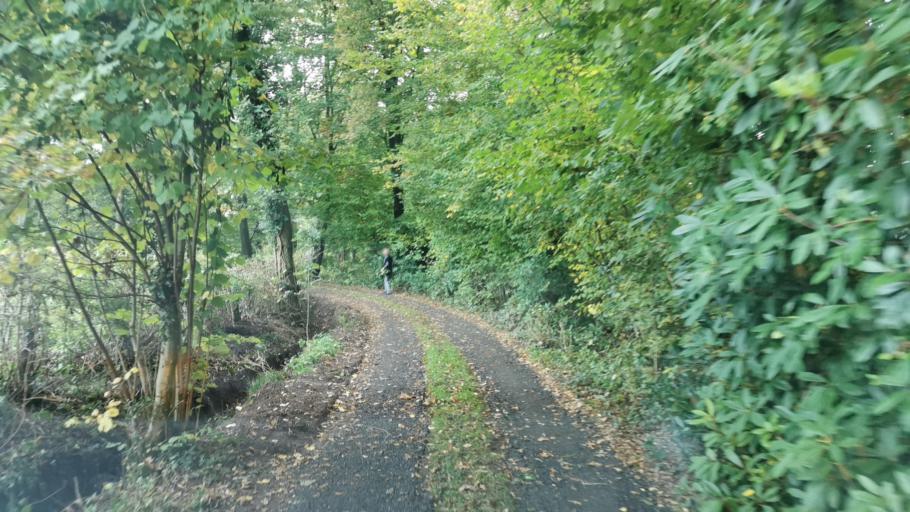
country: NL
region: Overijssel
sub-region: Gemeente Oldenzaal
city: Oldenzaal
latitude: 52.3086
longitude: 6.9513
